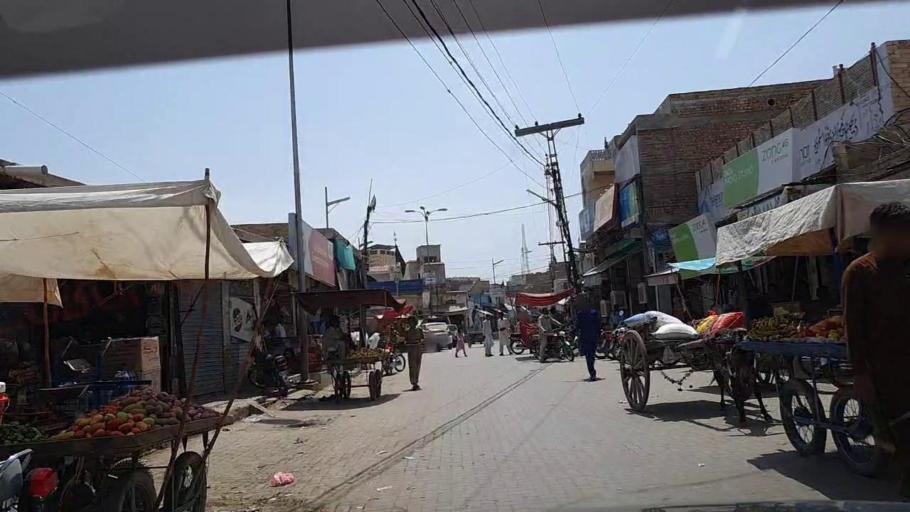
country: PK
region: Sindh
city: Khanpur
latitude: 27.8431
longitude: 69.4143
